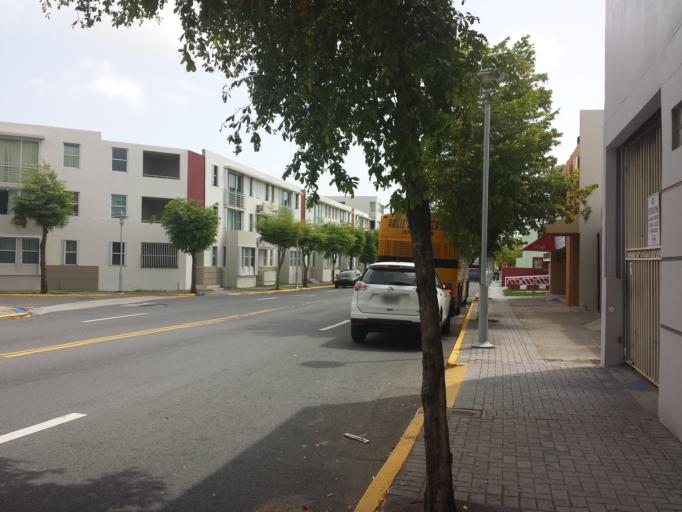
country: PR
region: Carolina
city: Carolina
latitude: 18.3824
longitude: -65.9554
